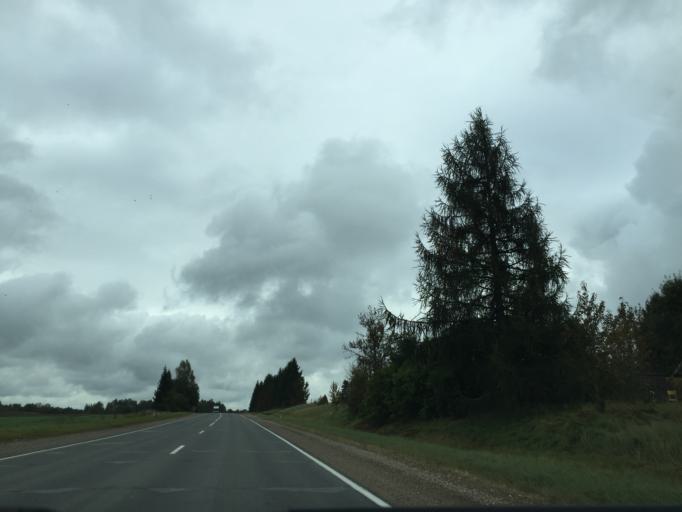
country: LV
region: Vilanu
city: Vilani
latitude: 56.5767
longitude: 26.9040
